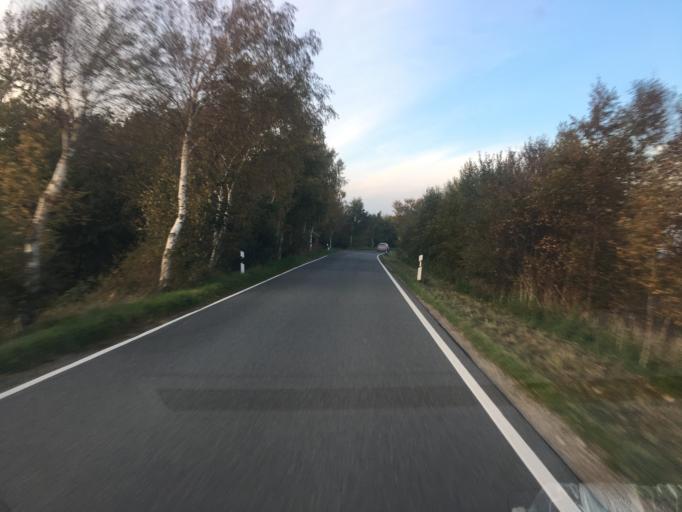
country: DE
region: Schleswig-Holstein
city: Humptrup
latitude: 54.8931
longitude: 8.8482
